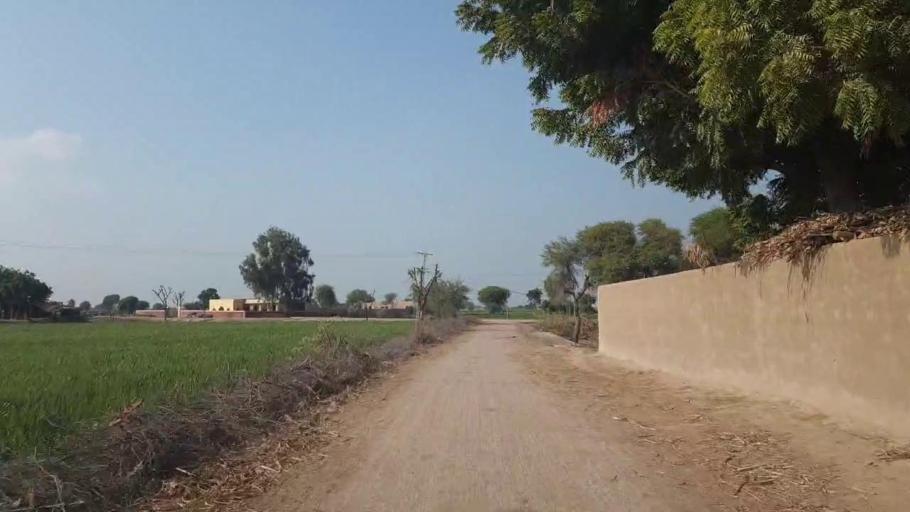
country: PK
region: Sindh
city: Hala
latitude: 25.8320
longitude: 68.3995
